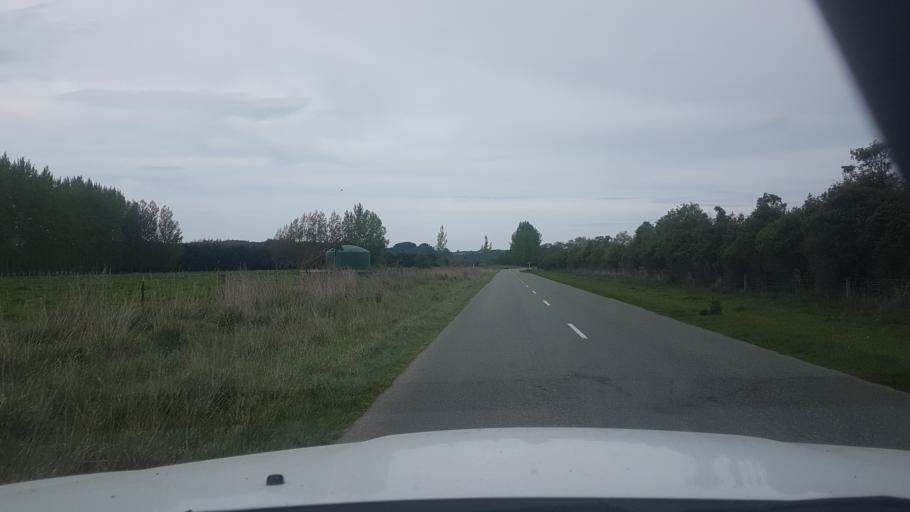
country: NZ
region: Canterbury
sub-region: Timaru District
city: Pleasant Point
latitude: -44.0738
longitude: 171.1679
